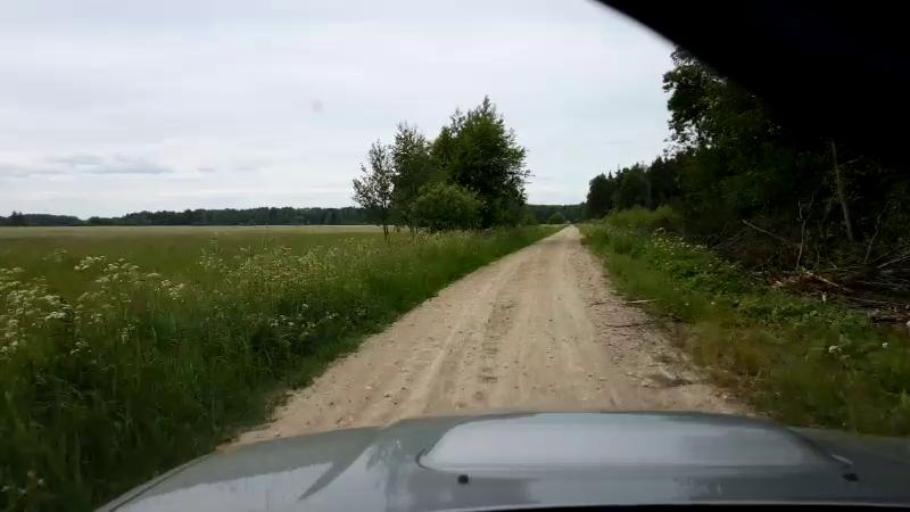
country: EE
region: Paernumaa
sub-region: Sindi linn
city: Sindi
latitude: 58.5132
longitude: 24.6197
